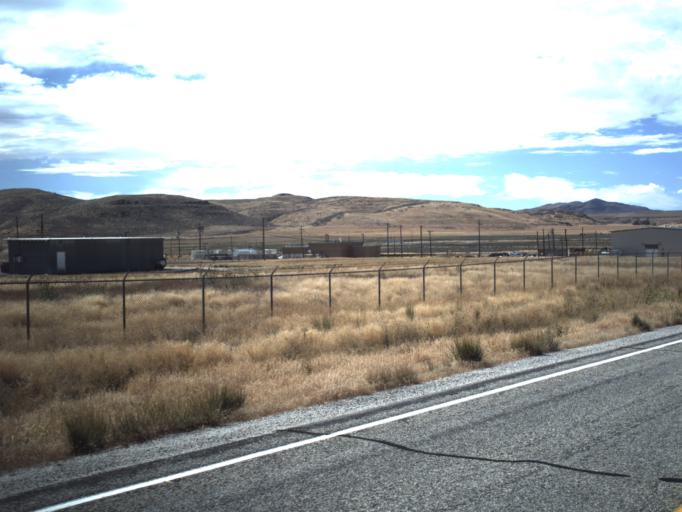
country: US
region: Utah
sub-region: Box Elder County
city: Tremonton
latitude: 41.7225
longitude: -112.4355
